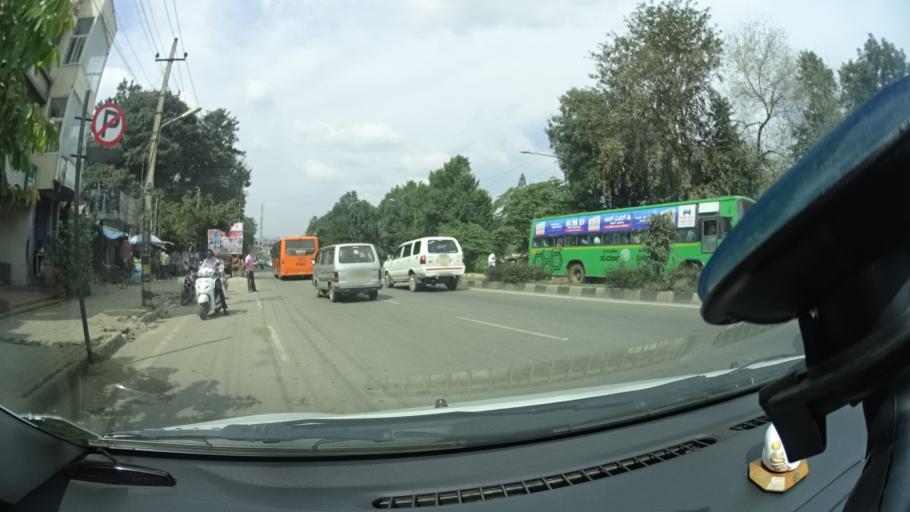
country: IN
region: Karnataka
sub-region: Bangalore Urban
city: Yelahanka
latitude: 13.1058
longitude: 77.5822
